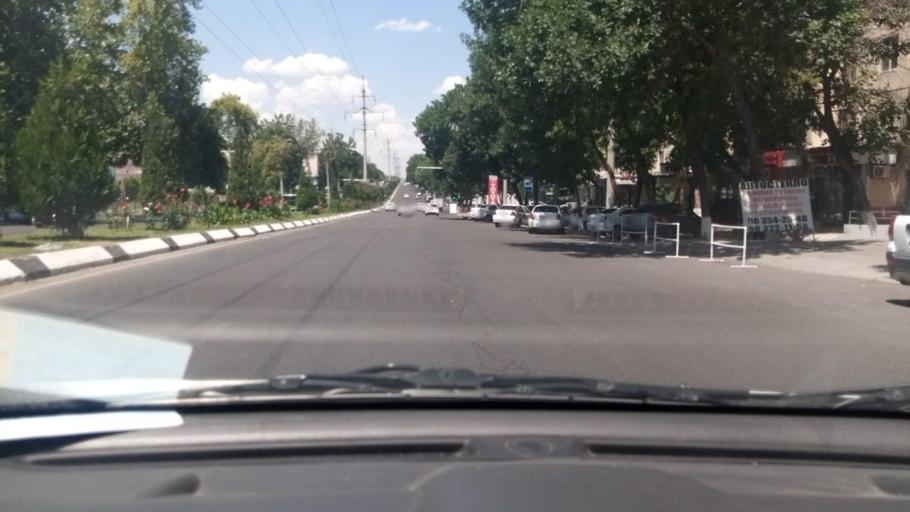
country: UZ
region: Toshkent Shahri
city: Tashkent
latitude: 41.2851
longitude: 69.1947
